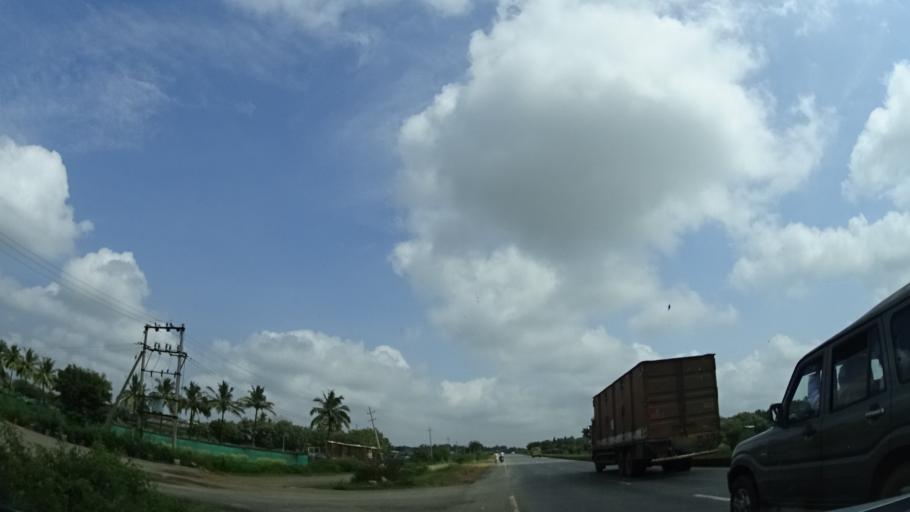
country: IN
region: Karnataka
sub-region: Dharwad
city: Hubli
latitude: 15.2774
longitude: 75.1470
